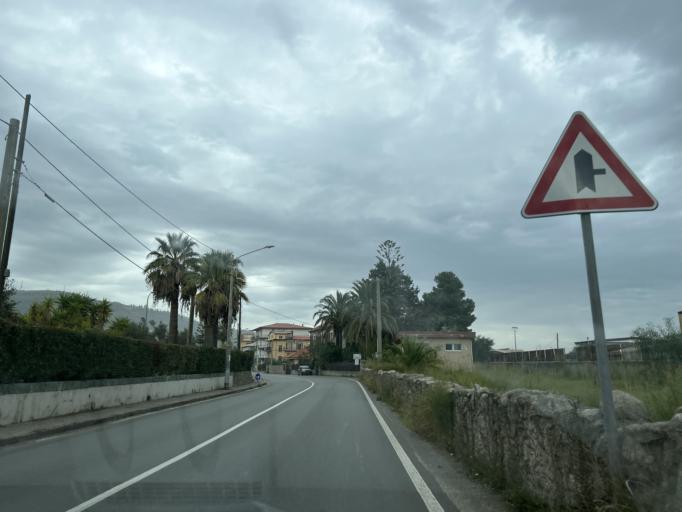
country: IT
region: Calabria
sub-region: Provincia di Catanzaro
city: Montepaone Lido
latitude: 38.7306
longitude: 16.5436
